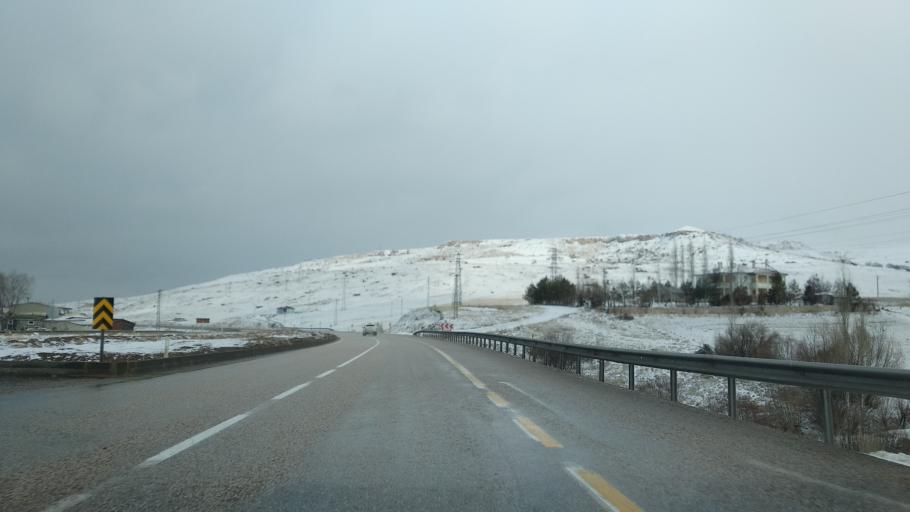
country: TR
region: Kayseri
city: Pinarbasi
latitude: 38.7005
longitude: 36.3696
